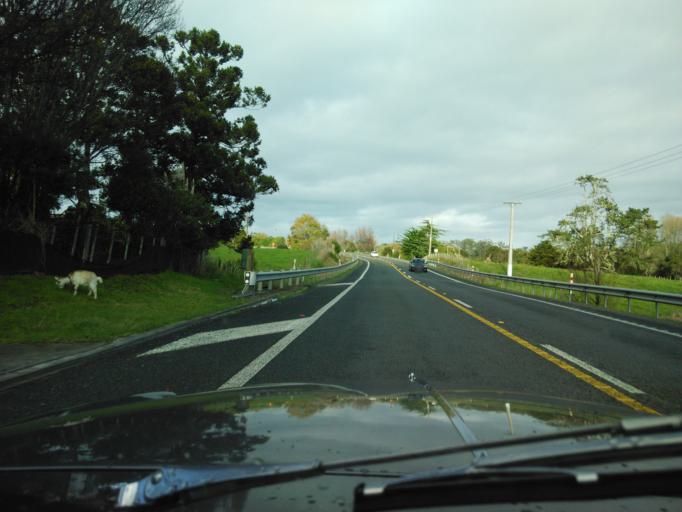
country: NZ
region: Auckland
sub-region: Auckland
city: Wellsford
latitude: -36.2454
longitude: 174.5085
